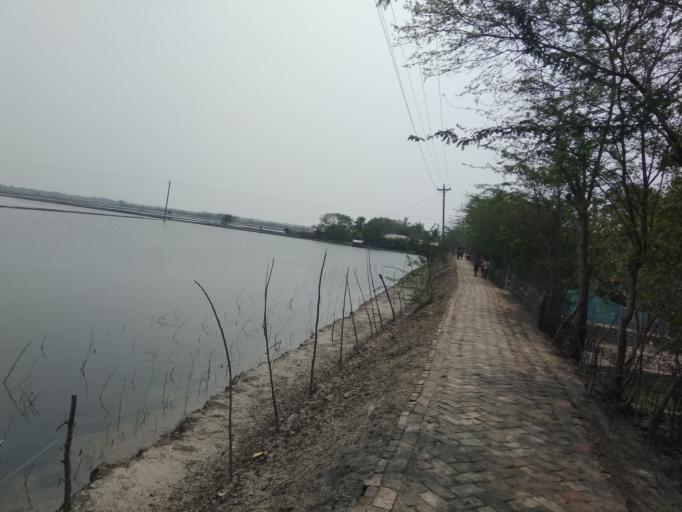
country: IN
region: West Bengal
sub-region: North 24 Parganas
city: Taki
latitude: 22.2807
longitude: 89.2946
